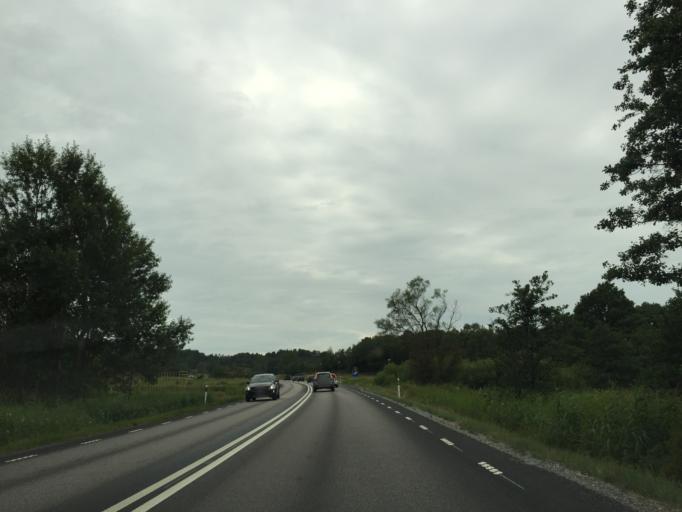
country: SE
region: Vaestra Goetaland
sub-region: Tjorns Kommun
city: Myggenas
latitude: 58.0469
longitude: 11.7478
